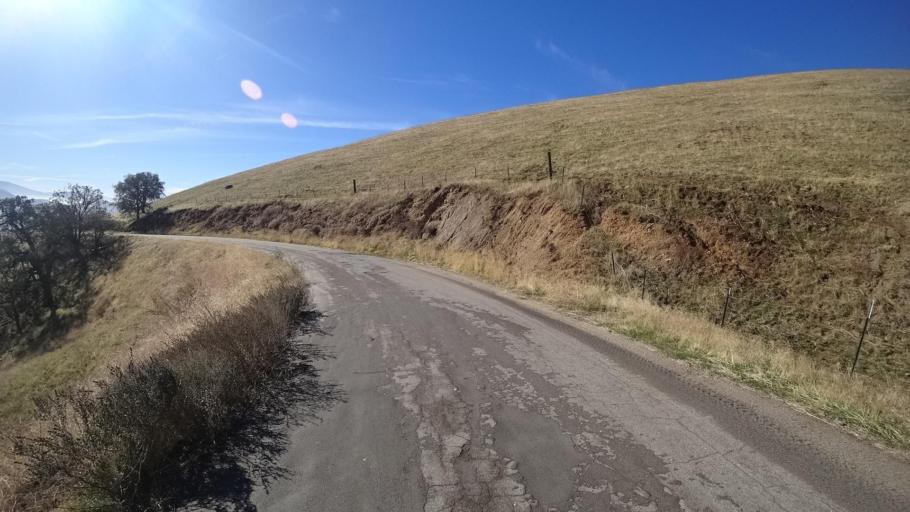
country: US
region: California
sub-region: Kern County
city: Arvin
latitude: 35.4265
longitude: -118.7300
